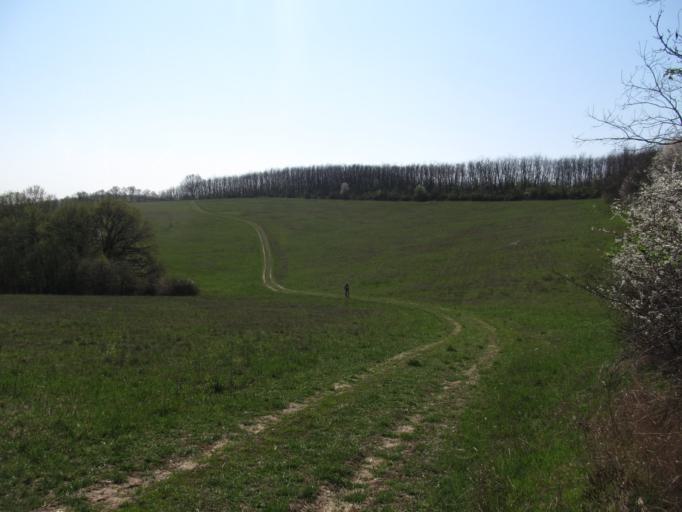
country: HU
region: Pest
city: Kosd
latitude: 47.8739
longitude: 19.1915
